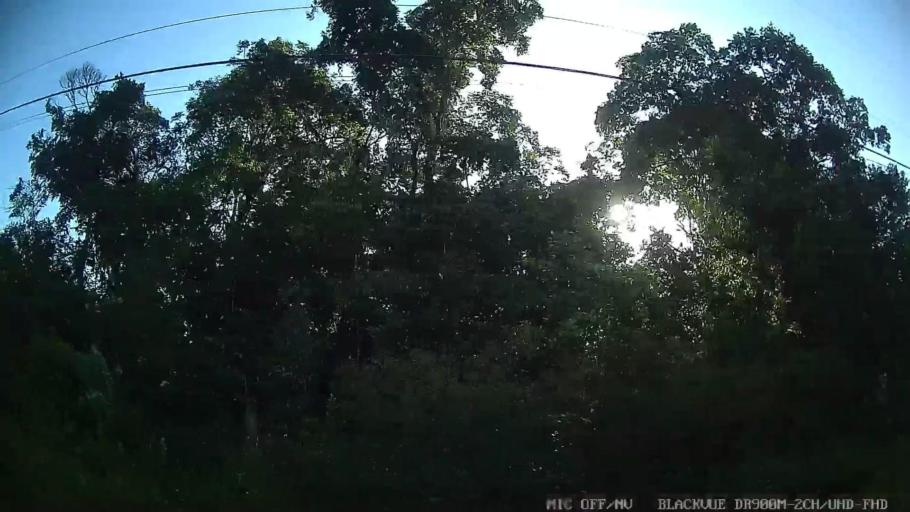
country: BR
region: Sao Paulo
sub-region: Itanhaem
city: Itanhaem
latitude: -24.2055
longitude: -46.8819
